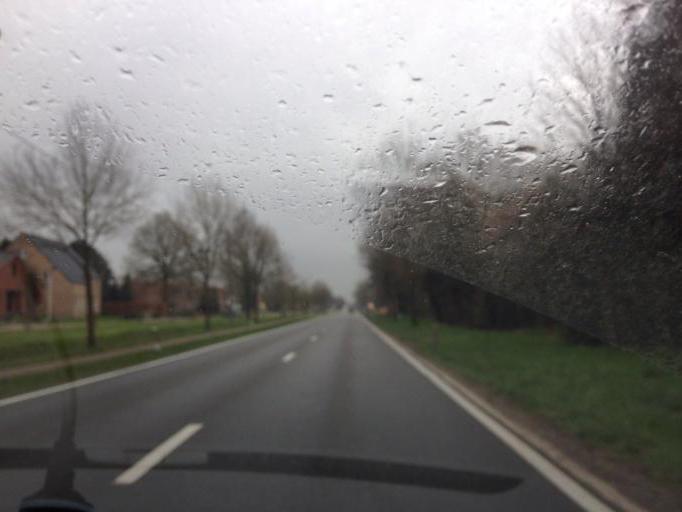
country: BE
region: Flanders
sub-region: Provincie Limburg
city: Opglabbeek
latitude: 51.0748
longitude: 5.5254
